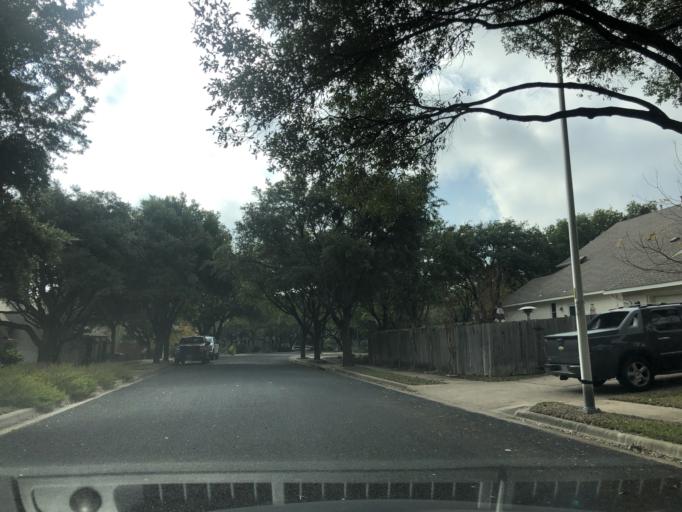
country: US
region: Texas
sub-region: Travis County
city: Wells Branch
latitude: 30.4179
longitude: -97.6828
